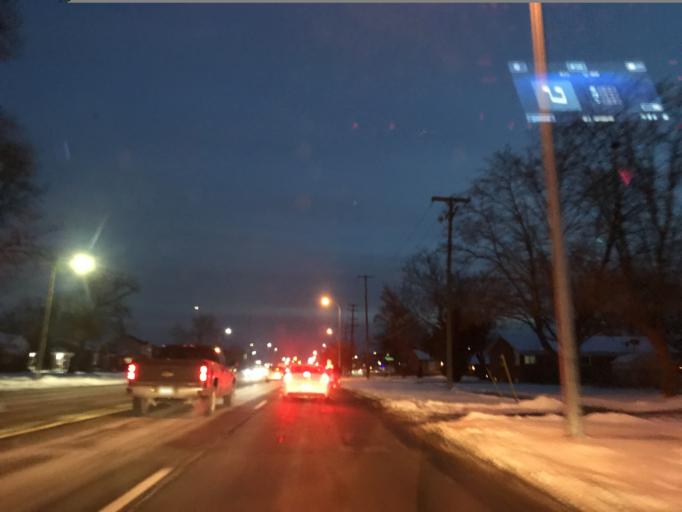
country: US
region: Michigan
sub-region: Wayne County
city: Redford
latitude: 42.3868
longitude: -83.3145
